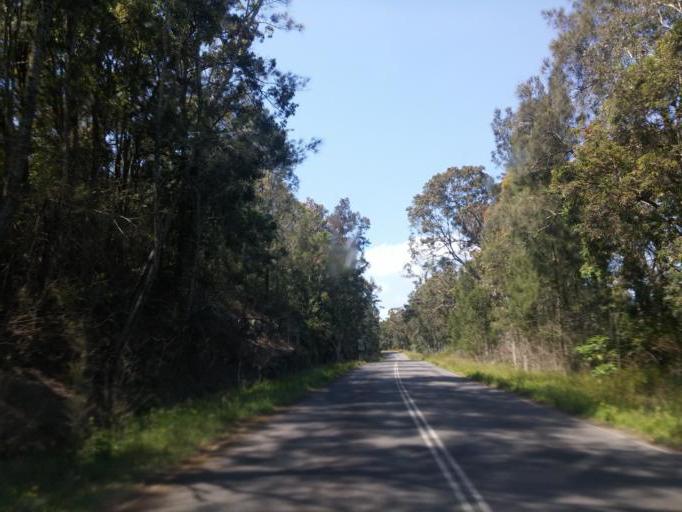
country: AU
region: New South Wales
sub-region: Great Lakes
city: Bulahdelah
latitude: -32.3901
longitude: 152.4295
